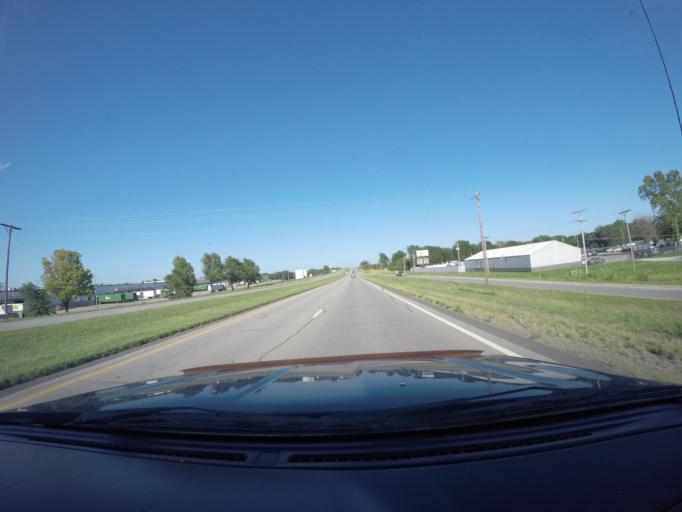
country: US
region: Kansas
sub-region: Shawnee County
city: Topeka
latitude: 39.0908
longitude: -95.6948
